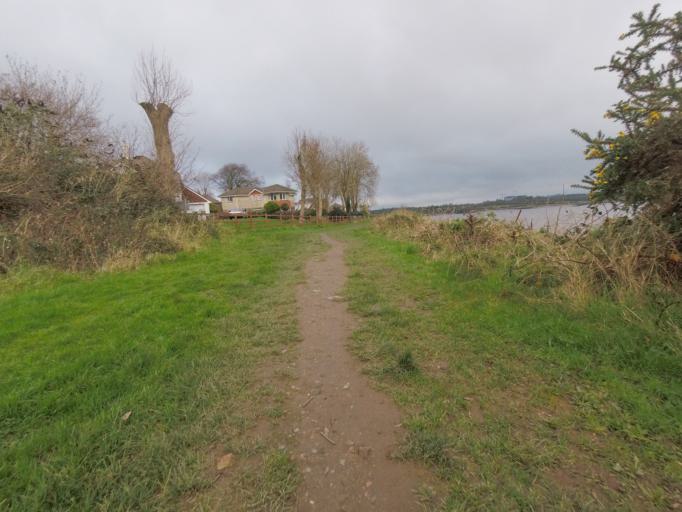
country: IE
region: Munster
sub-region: Waterford
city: Waterford
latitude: 52.2513
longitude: -7.0679
